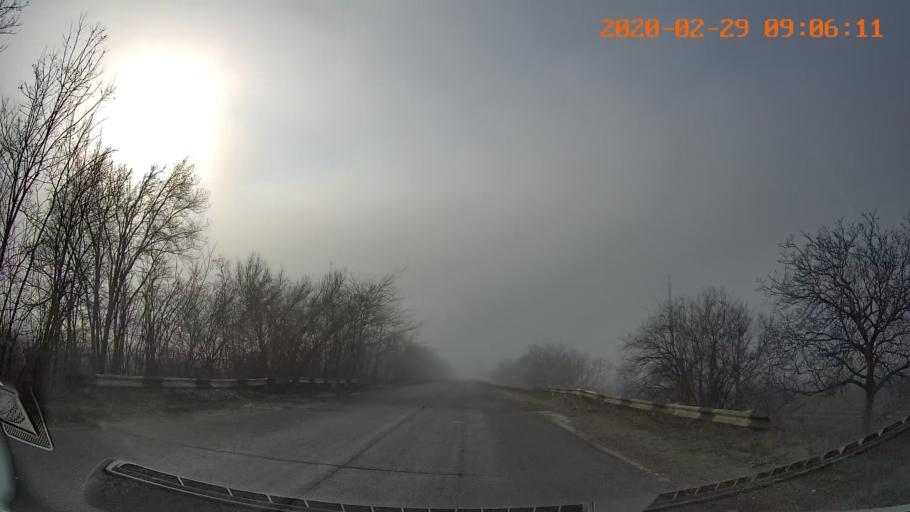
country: MD
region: Telenesti
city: Tiraspolul Nou
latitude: 46.8791
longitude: 29.7435
